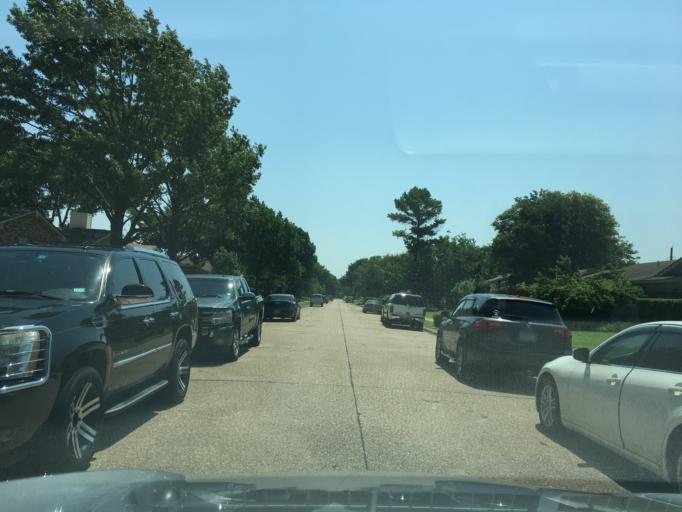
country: US
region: Texas
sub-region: Dallas County
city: Richardson
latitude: 32.9234
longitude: -96.6872
